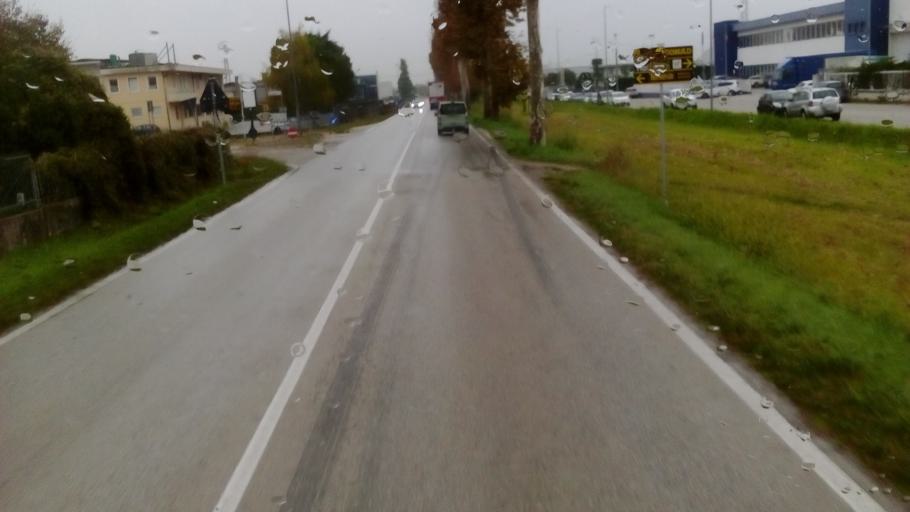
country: IT
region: Veneto
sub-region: Provincia di Vicenza
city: Sandrigo
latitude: 45.6581
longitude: 11.5813
